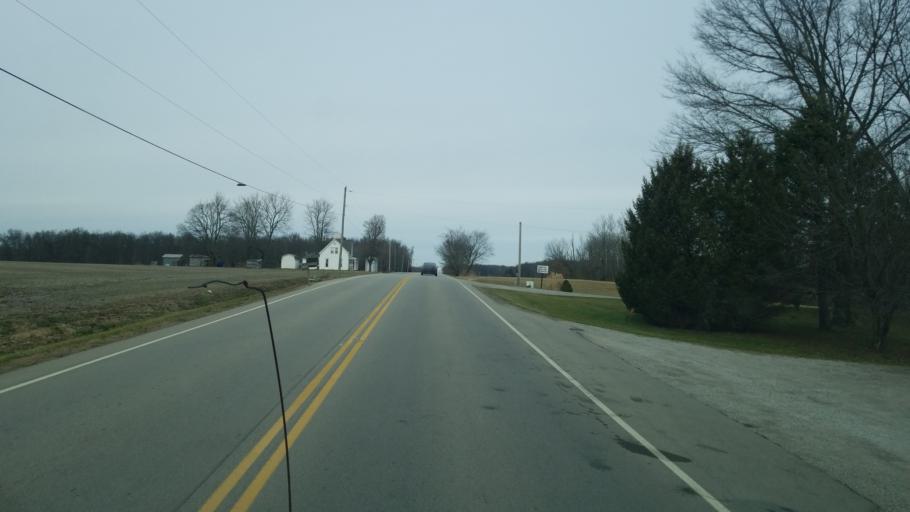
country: US
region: Ohio
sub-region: Adams County
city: Winchester
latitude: 39.0391
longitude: -83.7041
